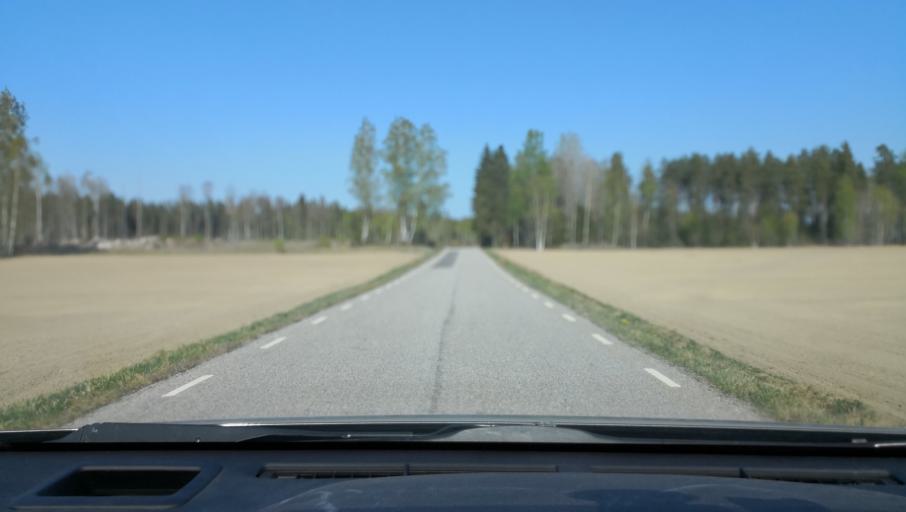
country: SE
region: Uppsala
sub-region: Heby Kommun
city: Heby
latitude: 60.0413
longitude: 16.8346
